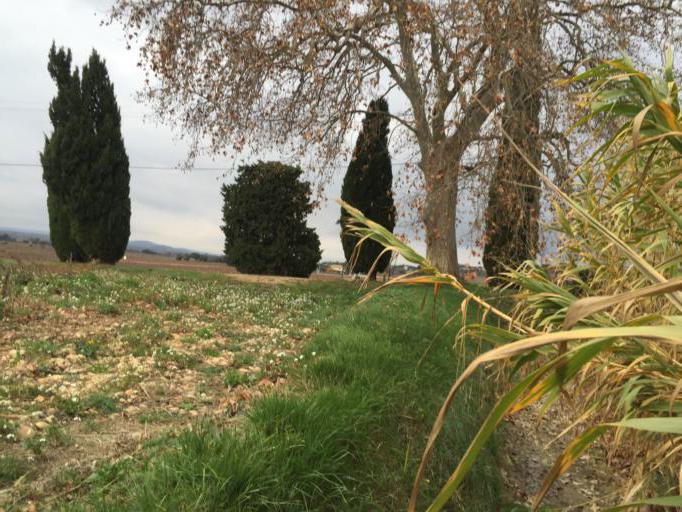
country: FR
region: Provence-Alpes-Cote d'Azur
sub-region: Departement du Vaucluse
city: Chateauneuf-du-Pape
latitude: 44.0451
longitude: 4.8499
